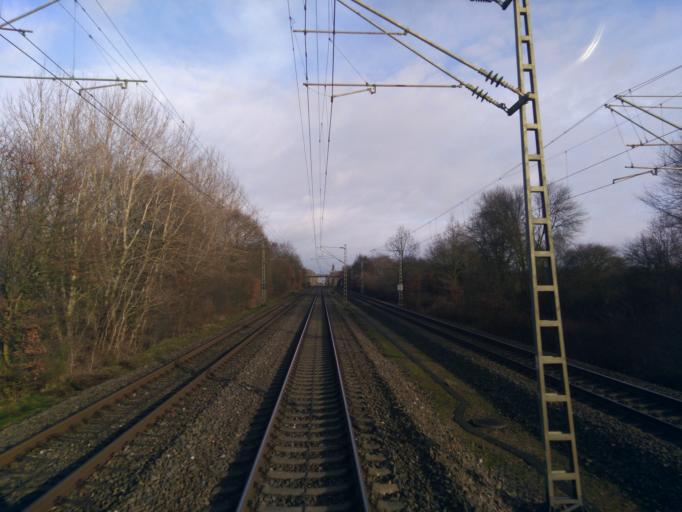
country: DE
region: Lower Saxony
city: Vahlde
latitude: 53.2138
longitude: 9.6063
